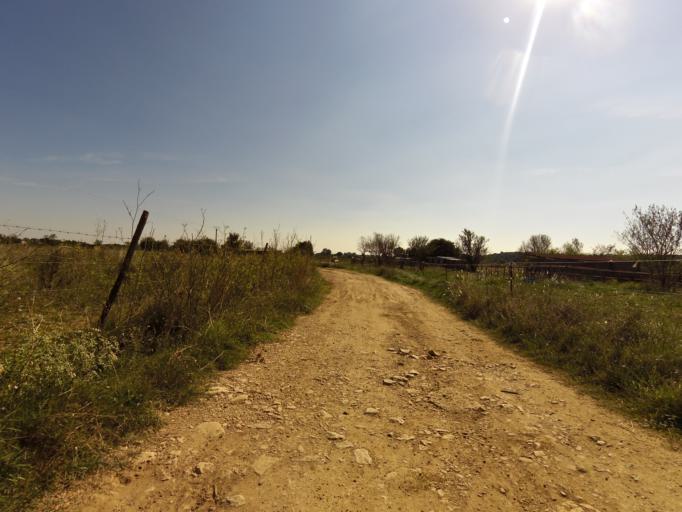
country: FR
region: Languedoc-Roussillon
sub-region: Departement du Gard
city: Gallargues-le-Montueux
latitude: 43.7235
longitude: 4.1575
